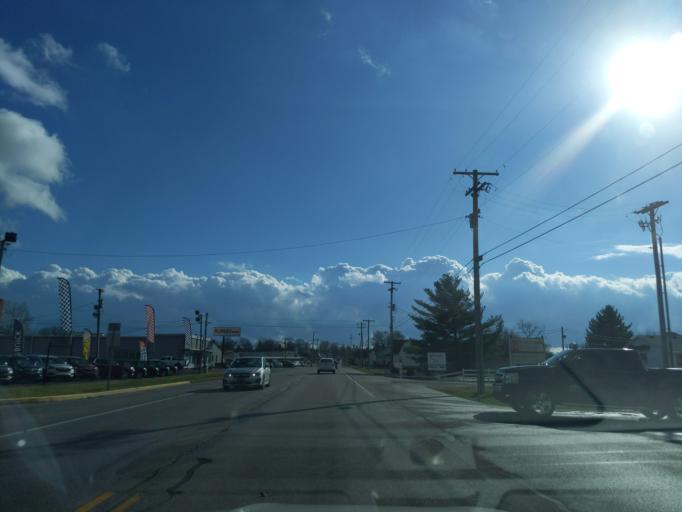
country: US
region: Indiana
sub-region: Decatur County
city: Greensburg
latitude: 39.3462
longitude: -85.4951
